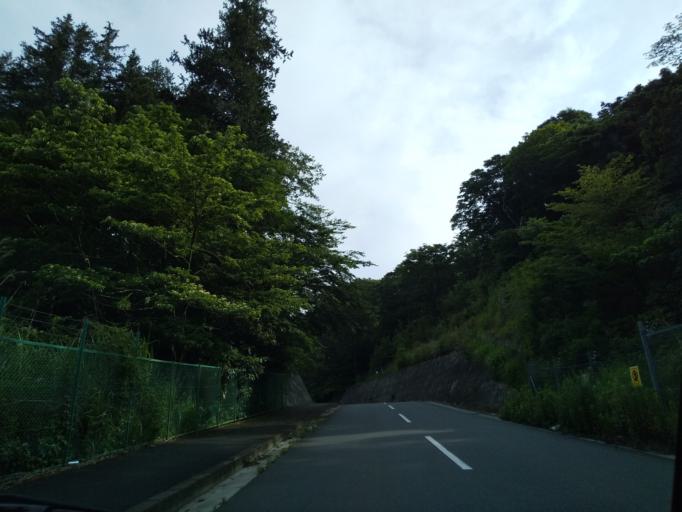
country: JP
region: Kanagawa
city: Atsugi
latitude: 35.4868
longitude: 139.3059
